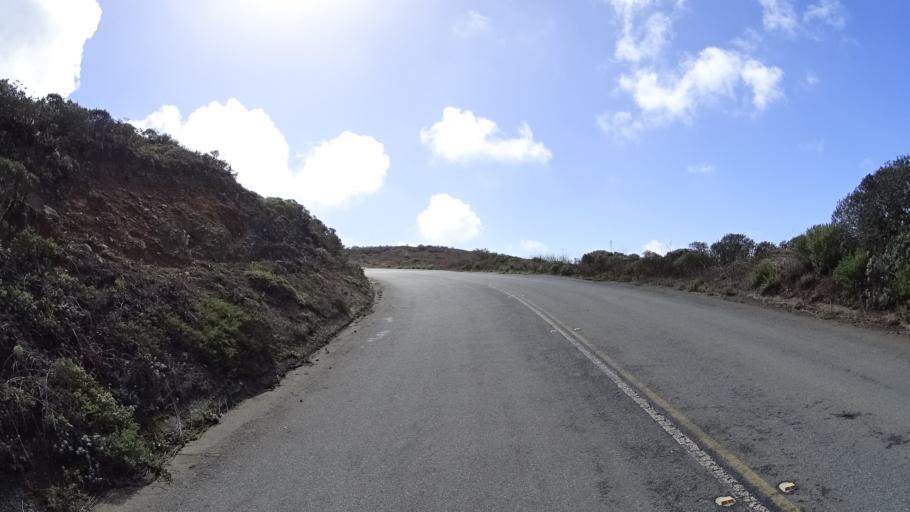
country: US
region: California
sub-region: San Mateo County
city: Colma
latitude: 37.6904
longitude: -122.4401
